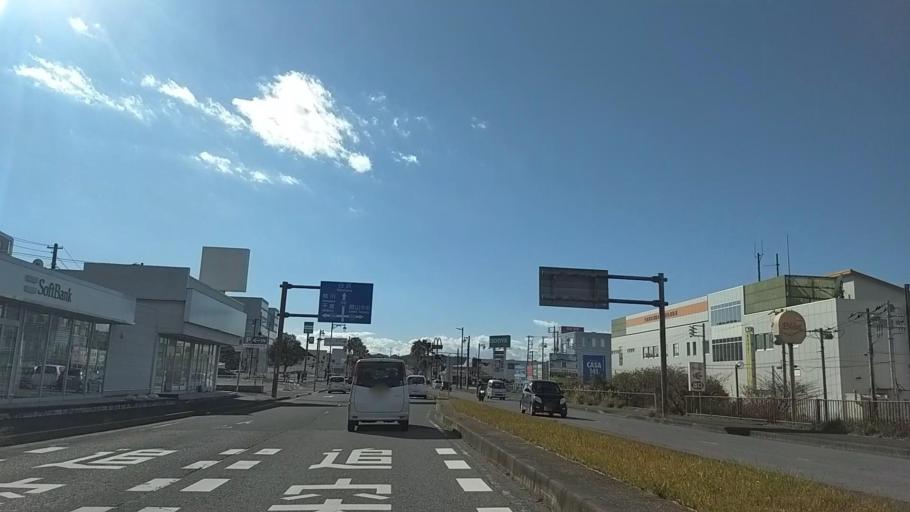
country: JP
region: Chiba
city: Tateyama
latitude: 34.9929
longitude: 139.8739
